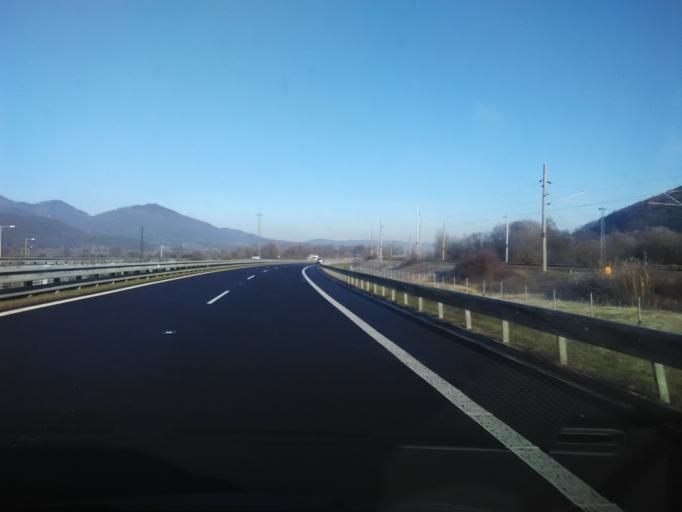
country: SK
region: Banskobystricky
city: Zarnovica
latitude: 48.5142
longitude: 18.7326
